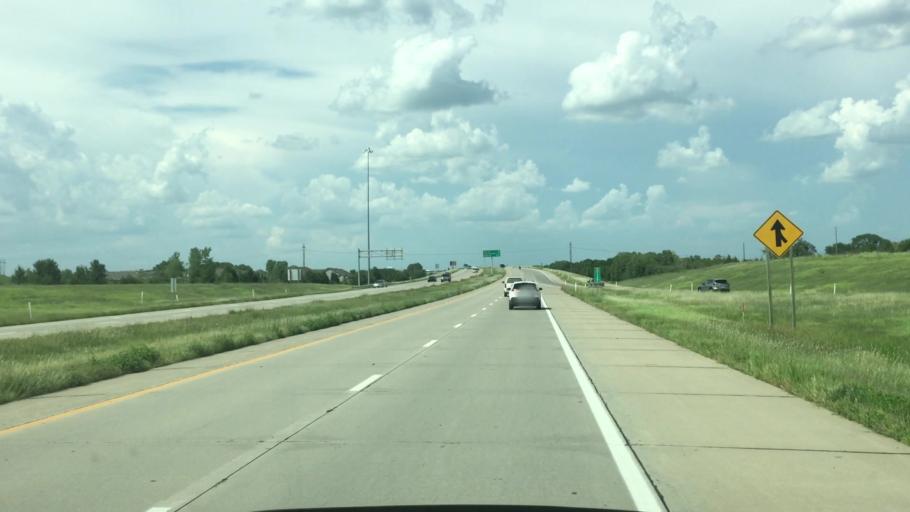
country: US
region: Kansas
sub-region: Butler County
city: Andover
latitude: 37.7103
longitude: -97.2001
